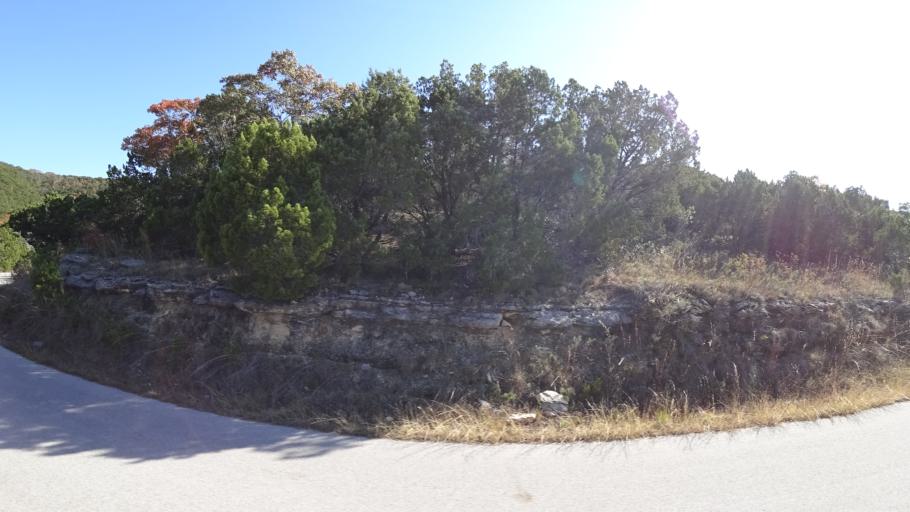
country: US
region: Texas
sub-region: Travis County
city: Hudson Bend
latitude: 30.3957
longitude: -97.8765
